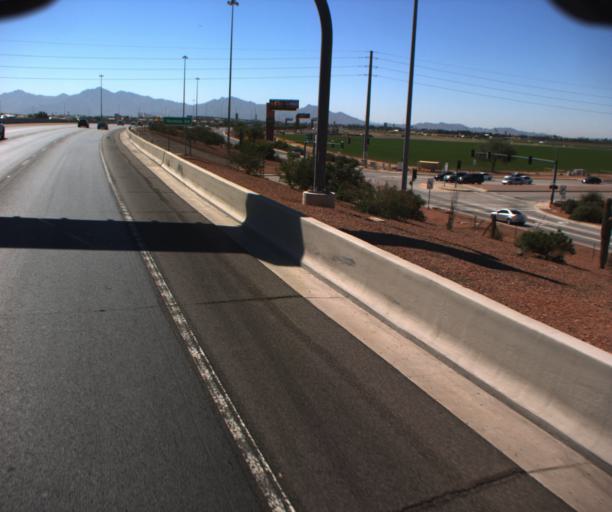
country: US
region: Arizona
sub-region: Maricopa County
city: Tolleson
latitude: 33.4802
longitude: -112.2640
